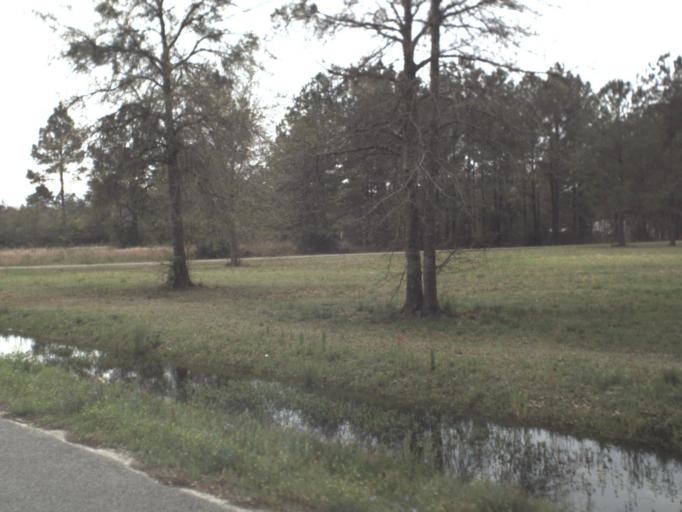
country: US
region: Florida
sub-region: Gulf County
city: Wewahitchka
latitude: 30.0353
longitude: -85.1829
